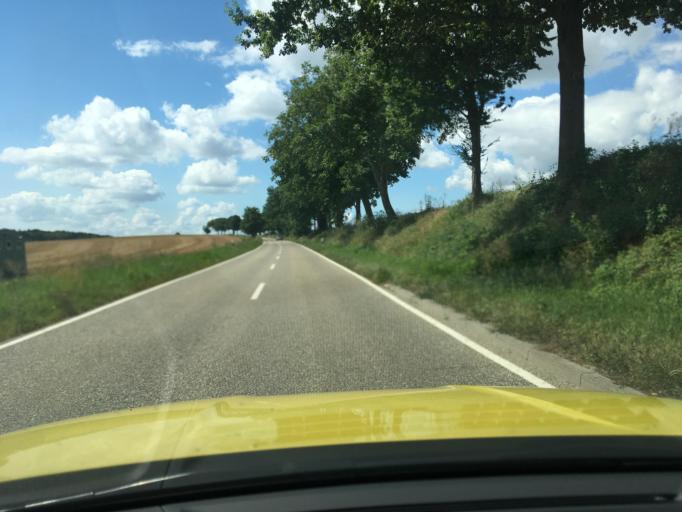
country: DE
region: Baden-Wuerttemberg
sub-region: Regierungsbezirk Stuttgart
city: Massenbachhausen
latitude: 49.1745
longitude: 9.0378
